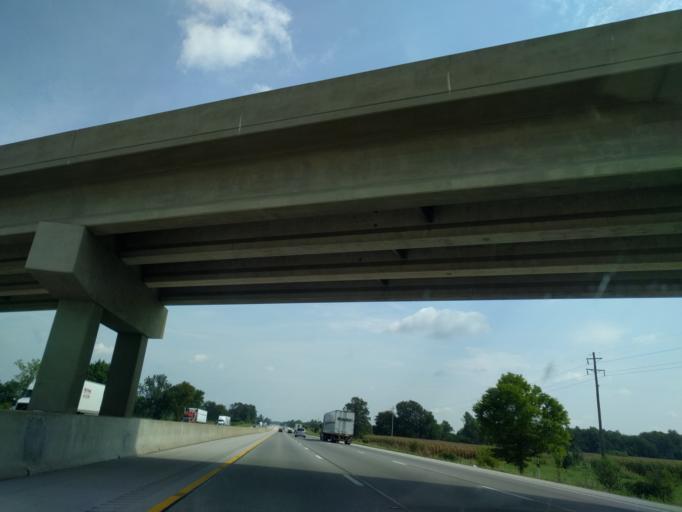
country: US
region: Kentucky
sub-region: Warren County
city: Plano
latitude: 36.8631
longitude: -86.4526
